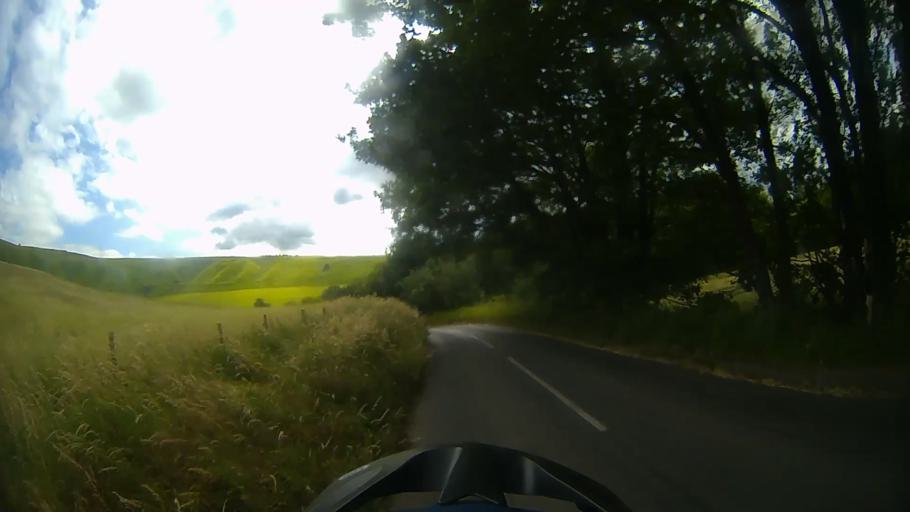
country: GB
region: England
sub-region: Oxfordshire
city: Faringdon
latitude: 51.5826
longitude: -1.5716
